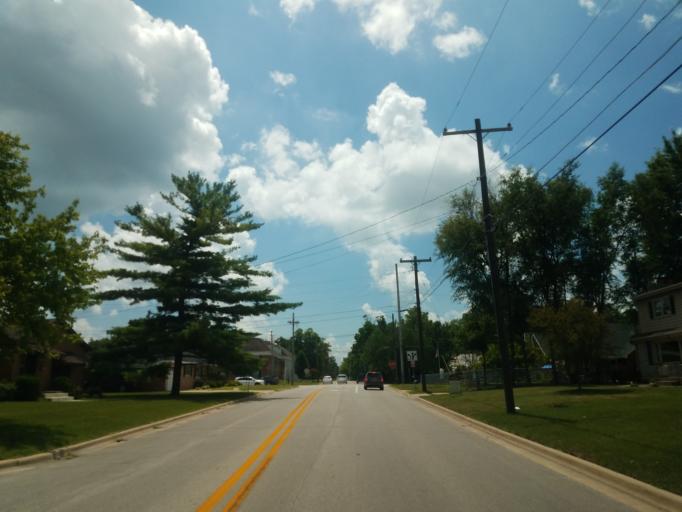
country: US
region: Illinois
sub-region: McLean County
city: Bloomington
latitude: 40.4746
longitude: -88.9629
